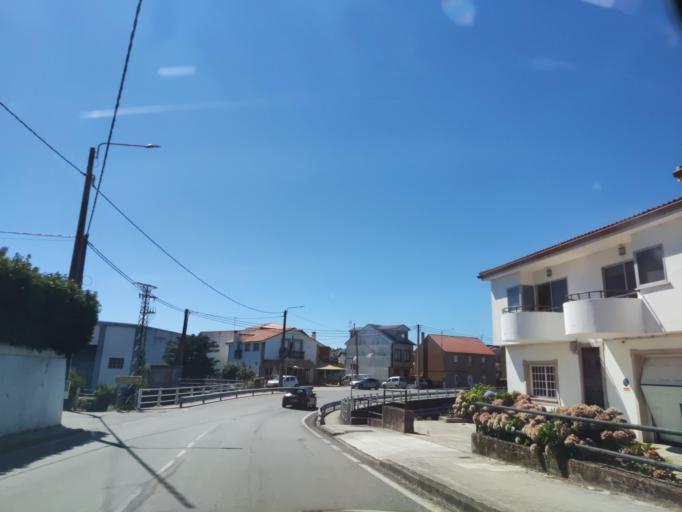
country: ES
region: Galicia
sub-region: Provincia da Coruna
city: Boiro
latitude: 42.6152
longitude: -8.9327
